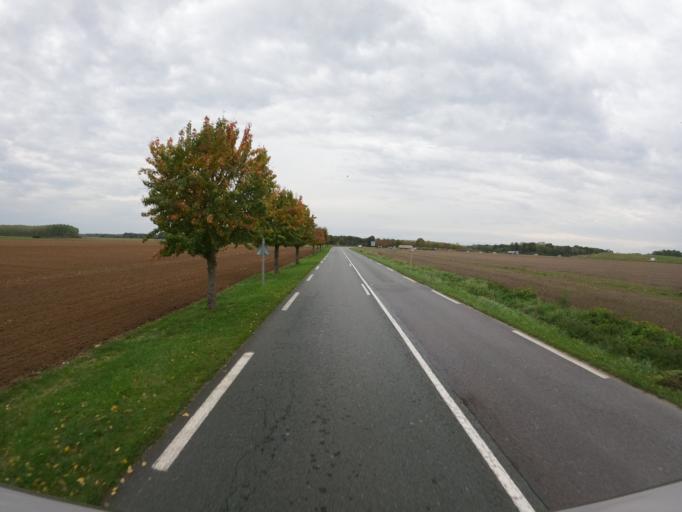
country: FR
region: Ile-de-France
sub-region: Departement de Seine-et-Marne
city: Villeneuve-le-Comte
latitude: 48.8168
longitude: 2.8226
